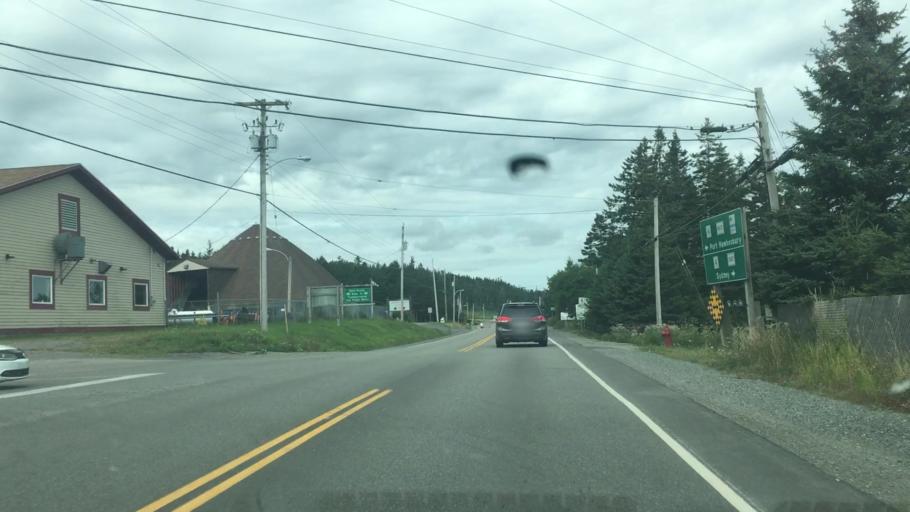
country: CA
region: Nova Scotia
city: Princeville
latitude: 45.6519
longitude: -60.8574
